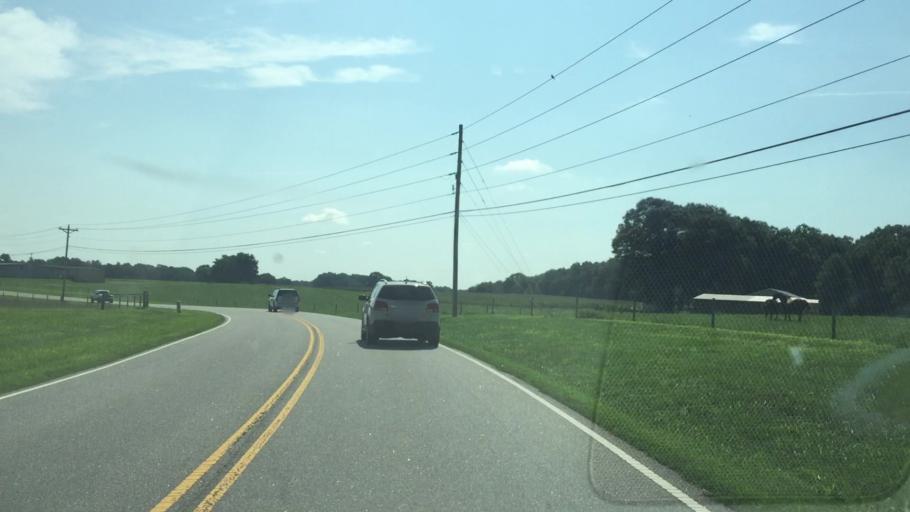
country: US
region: North Carolina
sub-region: Union County
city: Unionville
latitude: 35.1203
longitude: -80.4235
